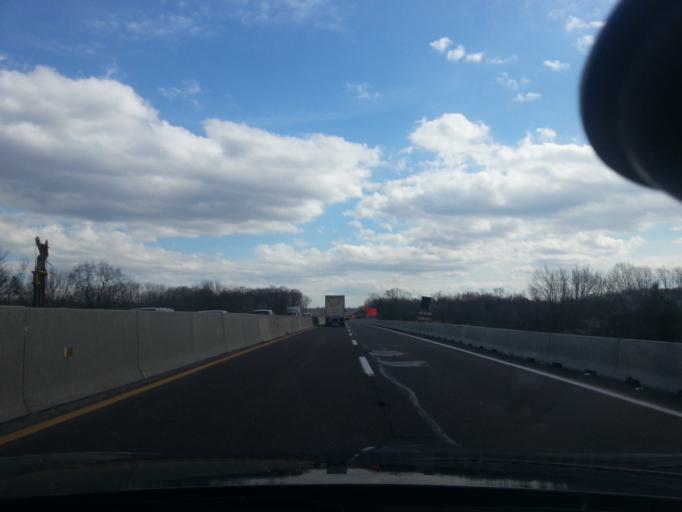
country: US
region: Pennsylvania
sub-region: Montgomery County
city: Kulpsville
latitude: 40.2369
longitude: -75.3394
